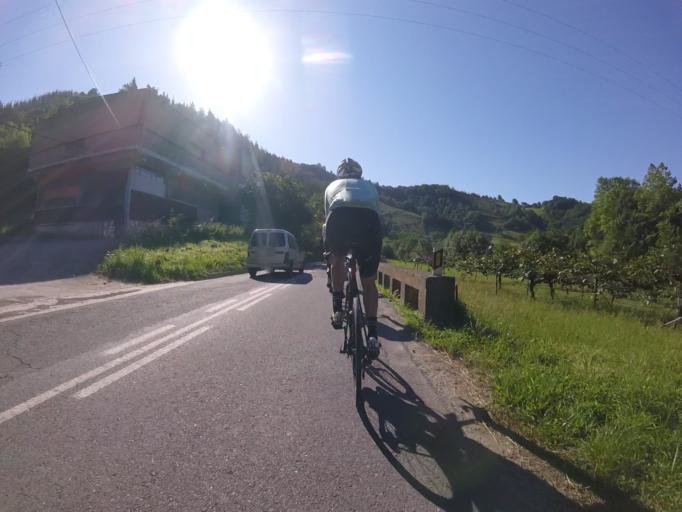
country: ES
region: Basque Country
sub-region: Provincia de Guipuzcoa
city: Beizama
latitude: 43.1482
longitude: -2.2354
